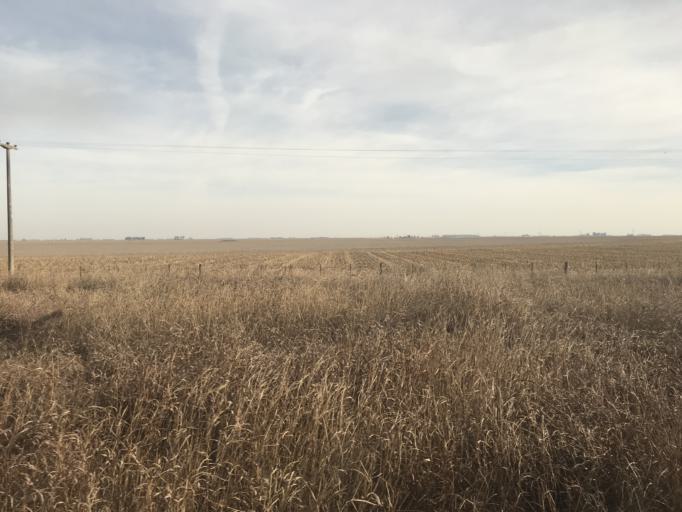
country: AR
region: Cordoba
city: Pilar
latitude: -31.7220
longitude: -63.8510
